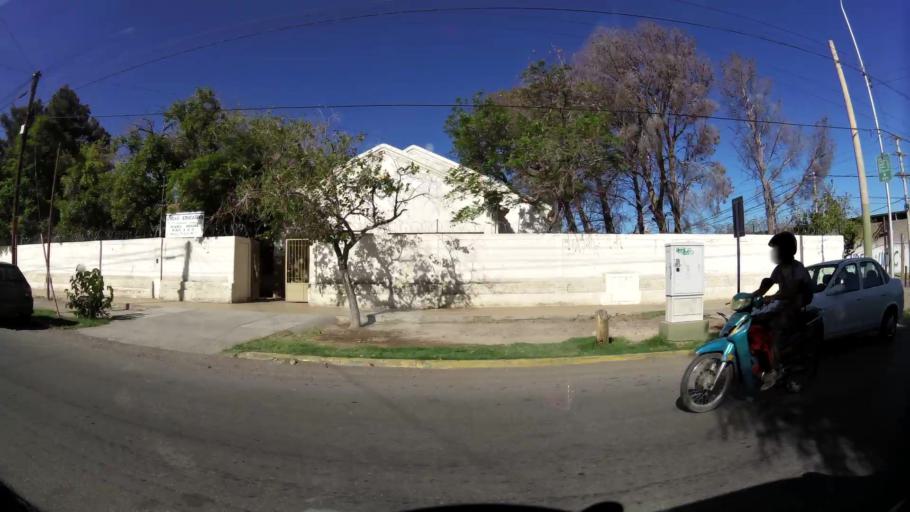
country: AR
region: San Juan
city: Villa Paula de Sarmiento
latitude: -31.5145
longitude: -68.5244
